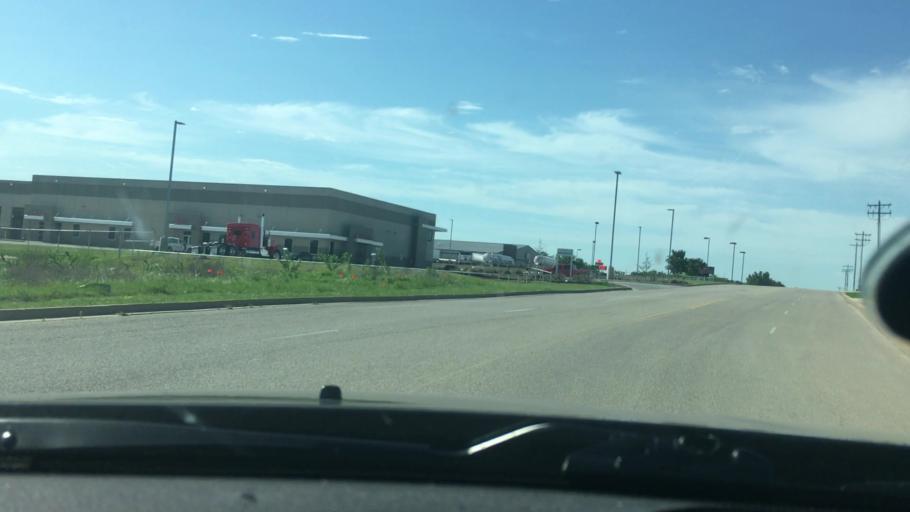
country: US
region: Oklahoma
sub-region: Carter County
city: Ardmore
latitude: 34.1982
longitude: -97.1672
